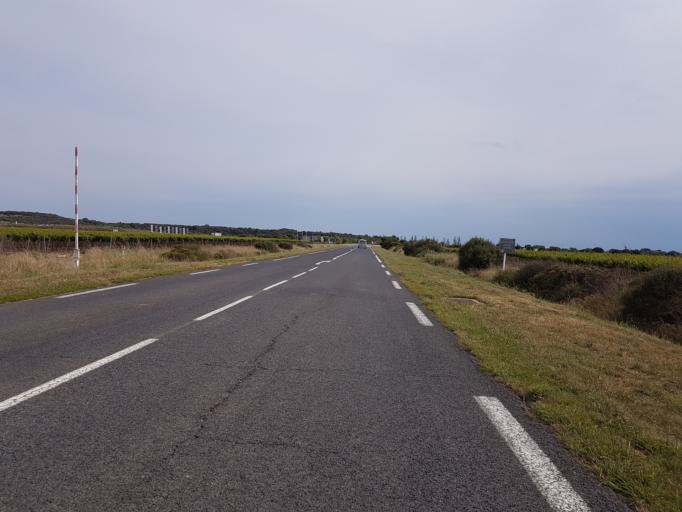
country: FR
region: Languedoc-Roussillon
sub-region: Departement de l'Herault
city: Portiragnes
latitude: 43.3168
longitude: 3.3603
